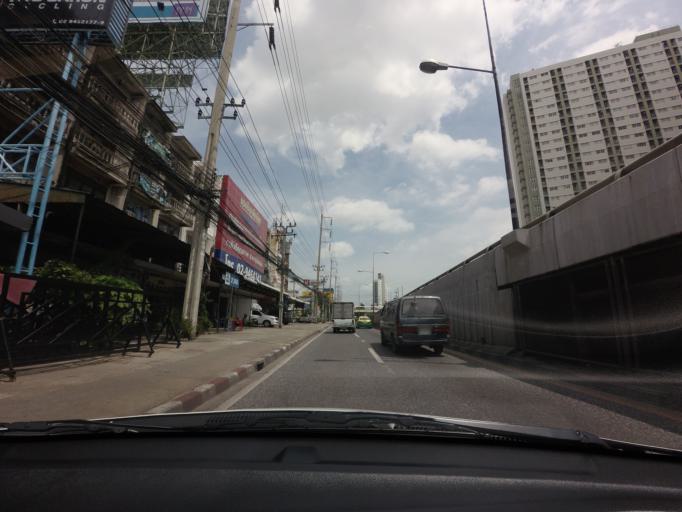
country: TH
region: Bangkok
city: Khan Na Yao
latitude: 13.8376
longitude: 100.6638
